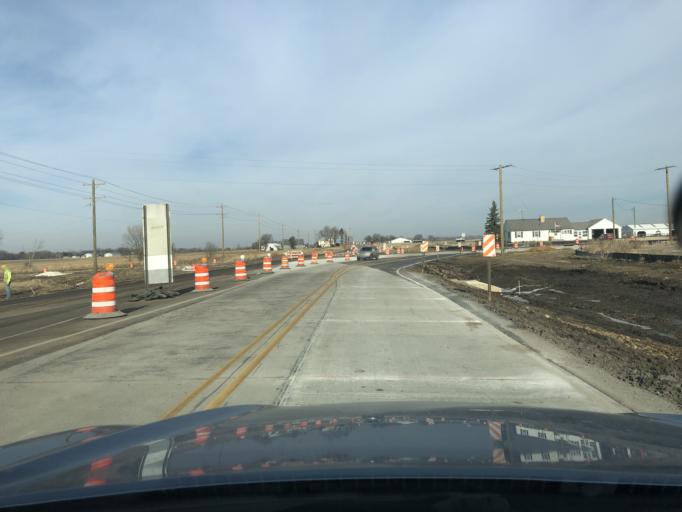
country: US
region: Illinois
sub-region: McHenry County
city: Marengo
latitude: 42.1814
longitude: -88.6179
